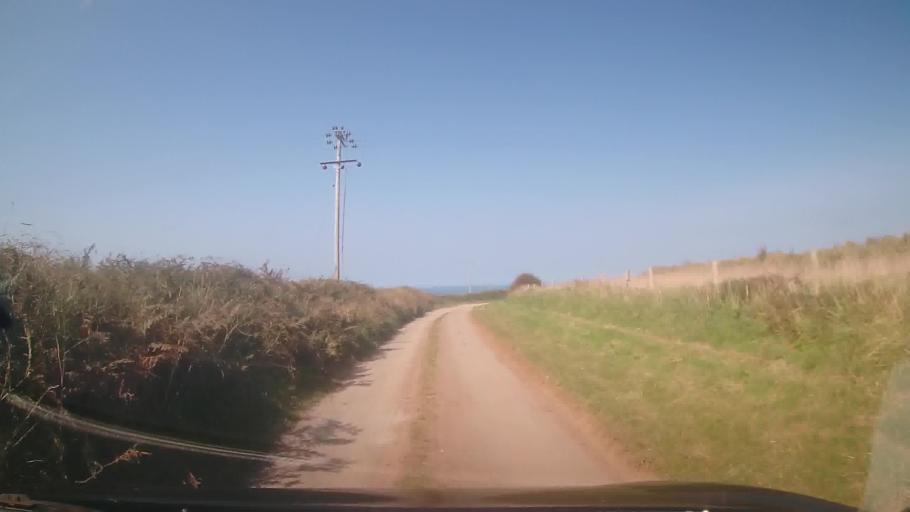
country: GB
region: Wales
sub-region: Pembrokeshire
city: Llanrhian
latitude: 51.9227
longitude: -5.2183
